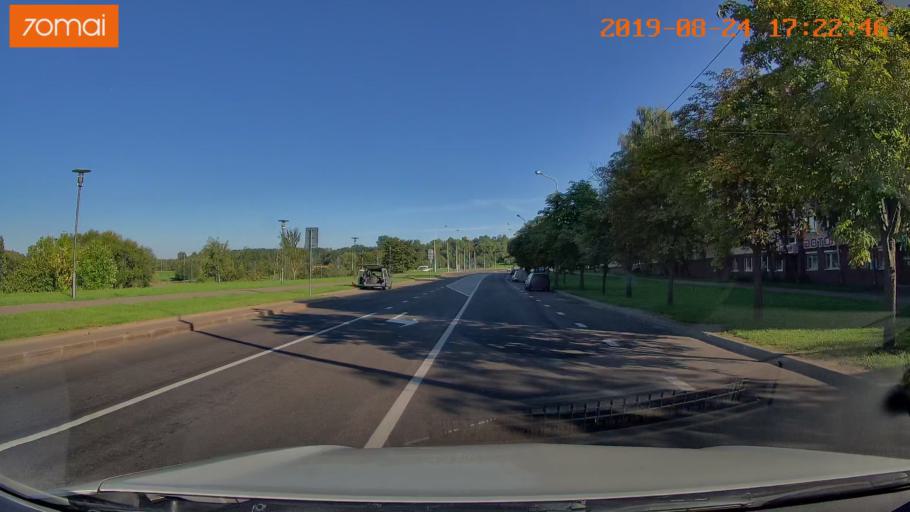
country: BY
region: Minsk
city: Hatava
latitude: 53.8442
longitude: 27.6477
